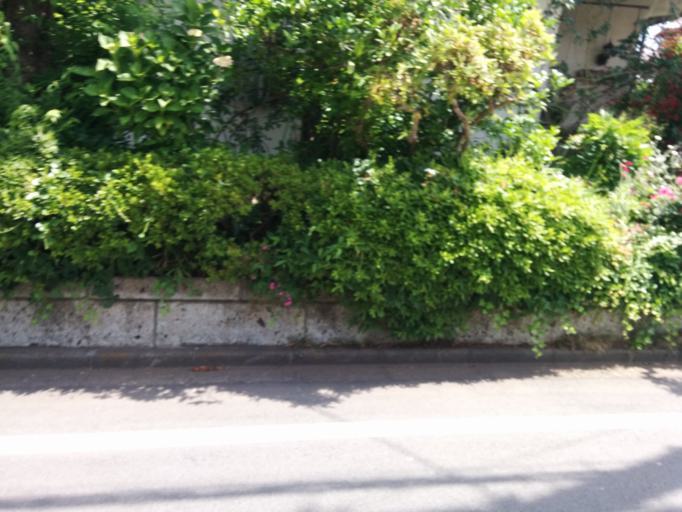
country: JP
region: Tokyo
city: Higashimurayama-shi
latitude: 35.7553
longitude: 139.4857
